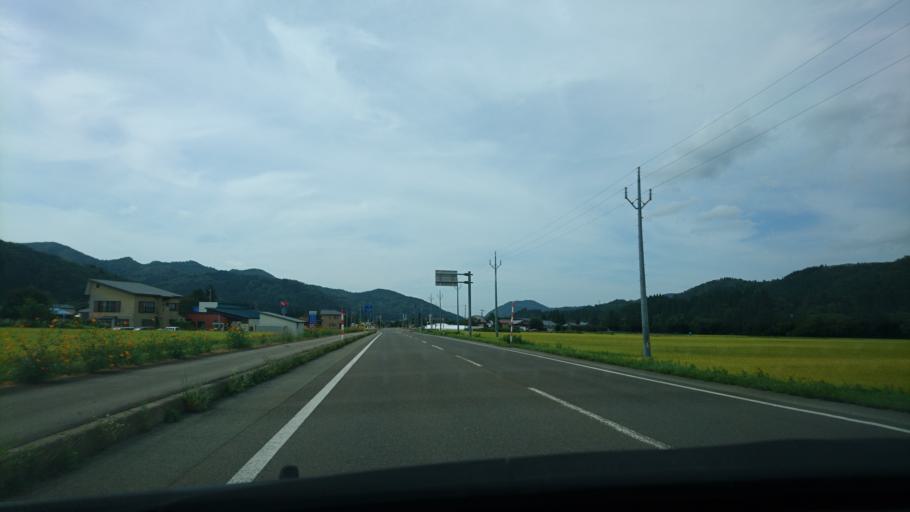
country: JP
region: Akita
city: Yuzawa
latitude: 39.1833
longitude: 140.6423
